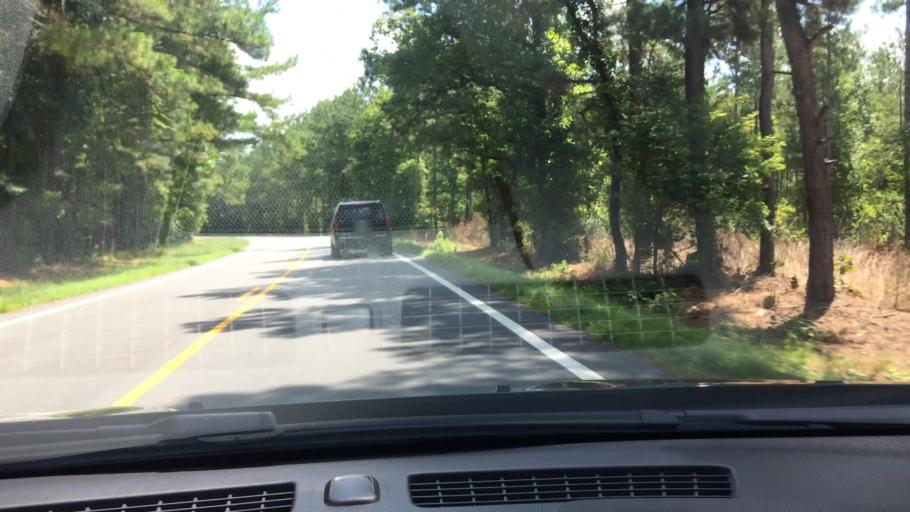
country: US
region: North Carolina
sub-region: Craven County
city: Vanceboro
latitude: 35.4244
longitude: -77.2170
